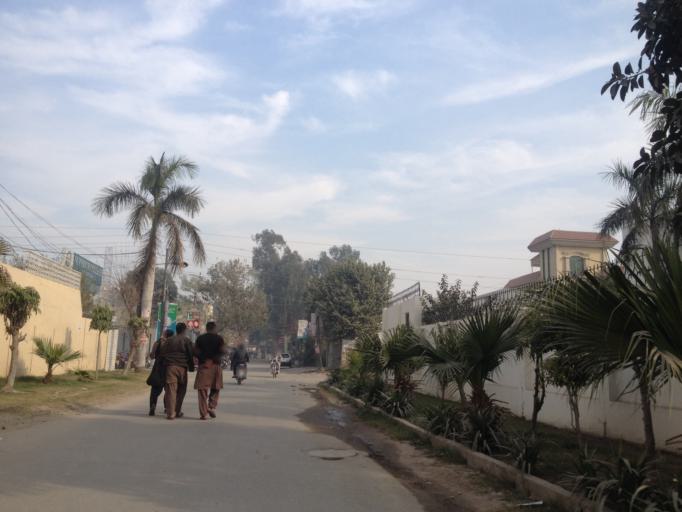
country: PK
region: Punjab
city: Lahore
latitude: 31.4653
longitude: 74.3089
